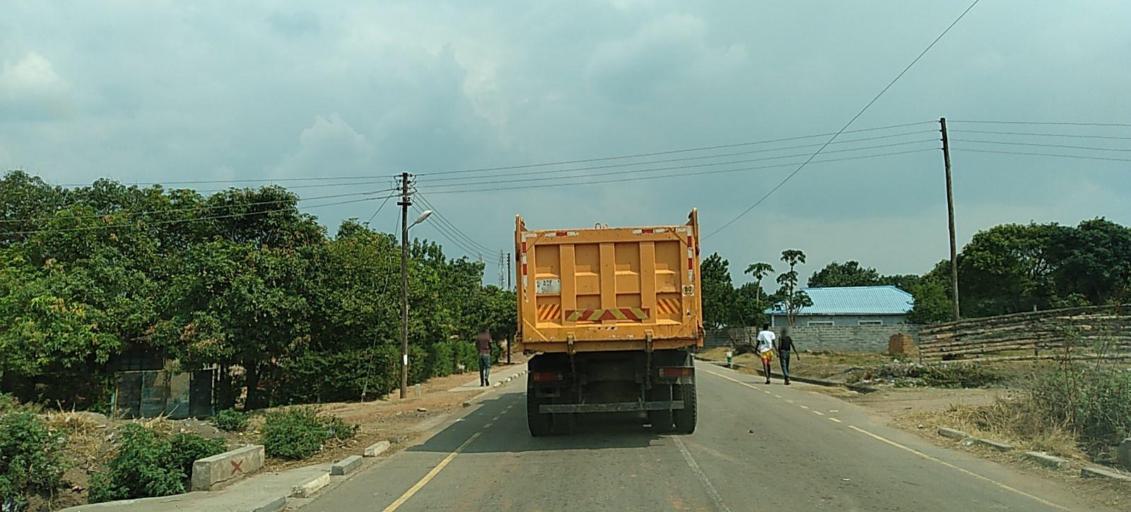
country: ZM
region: Copperbelt
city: Kalulushi
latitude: -12.8478
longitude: 28.1329
